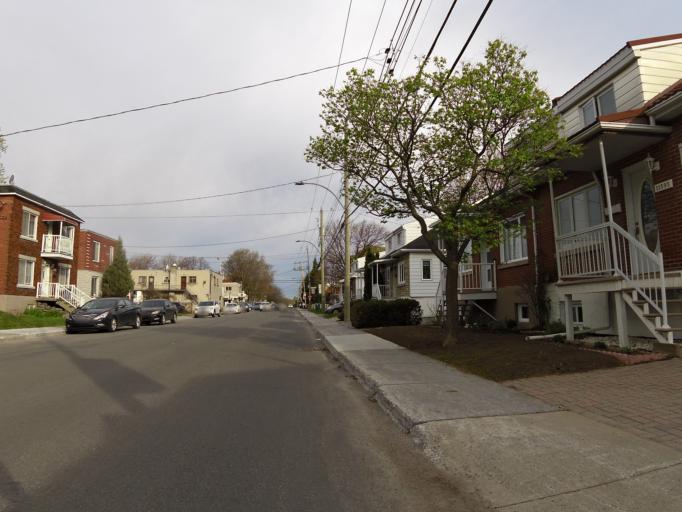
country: CA
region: Quebec
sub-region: Laval
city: Laval
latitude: 45.5402
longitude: -73.6858
